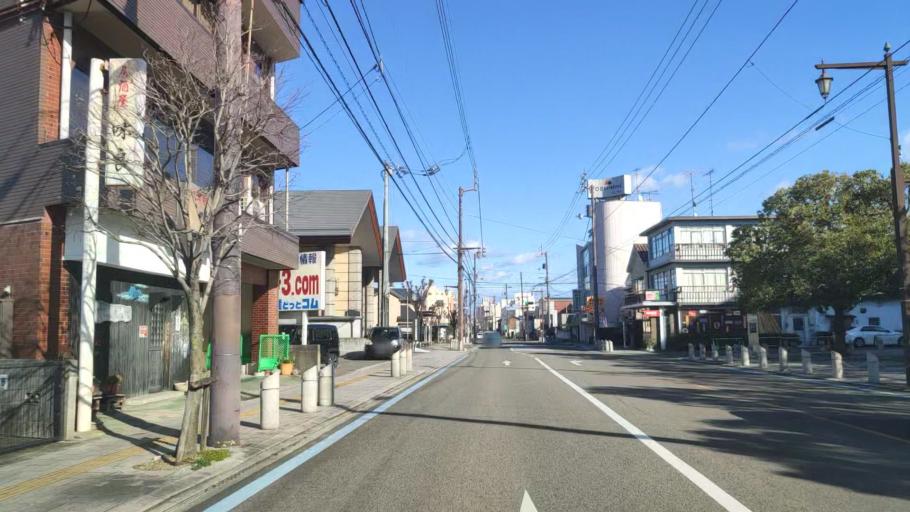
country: JP
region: Ehime
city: Saijo
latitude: 33.9120
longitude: 133.1822
